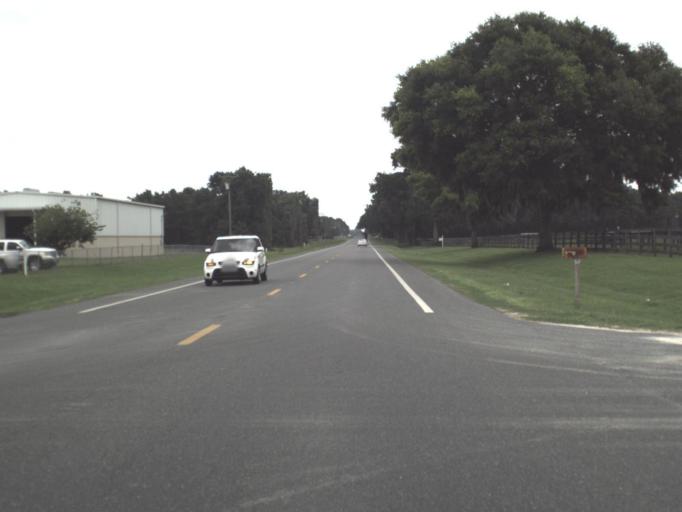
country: US
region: Florida
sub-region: Levy County
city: Williston
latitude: 29.3559
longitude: -82.4558
